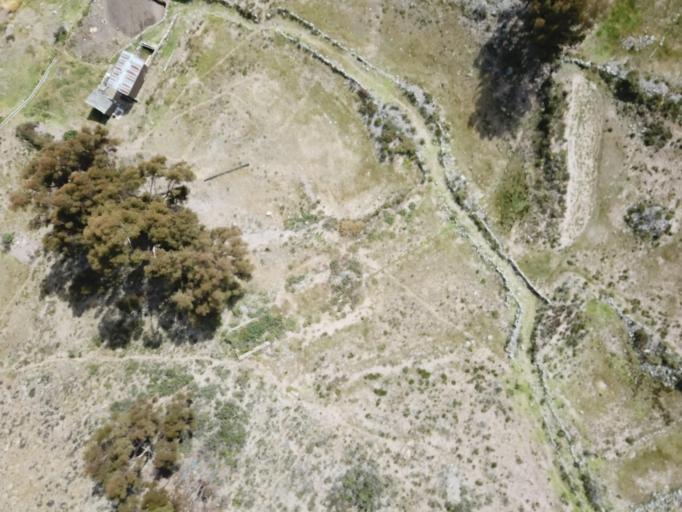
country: BO
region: La Paz
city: Achacachi
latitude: -16.0549
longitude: -68.8100
